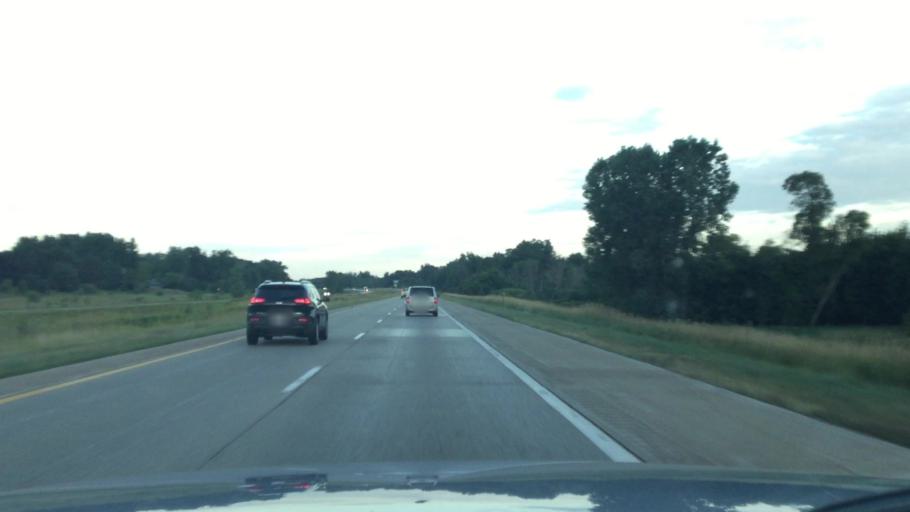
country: US
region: Michigan
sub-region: Shiawassee County
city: Perry
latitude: 42.8302
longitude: -84.2487
